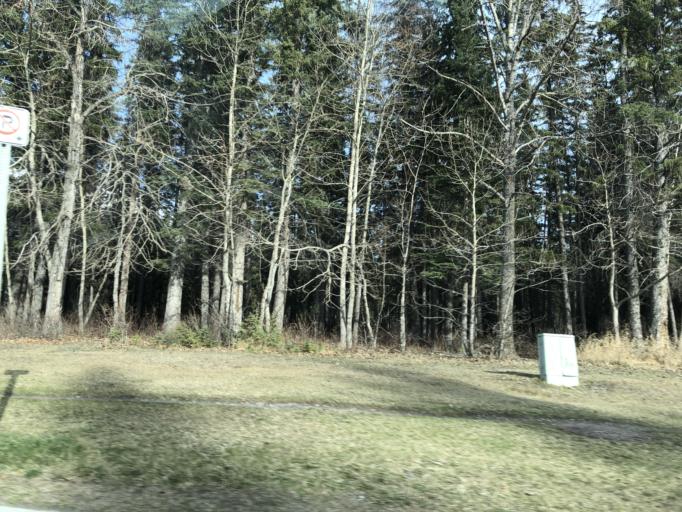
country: CA
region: Alberta
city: Canmore
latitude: 51.0847
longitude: -115.3672
